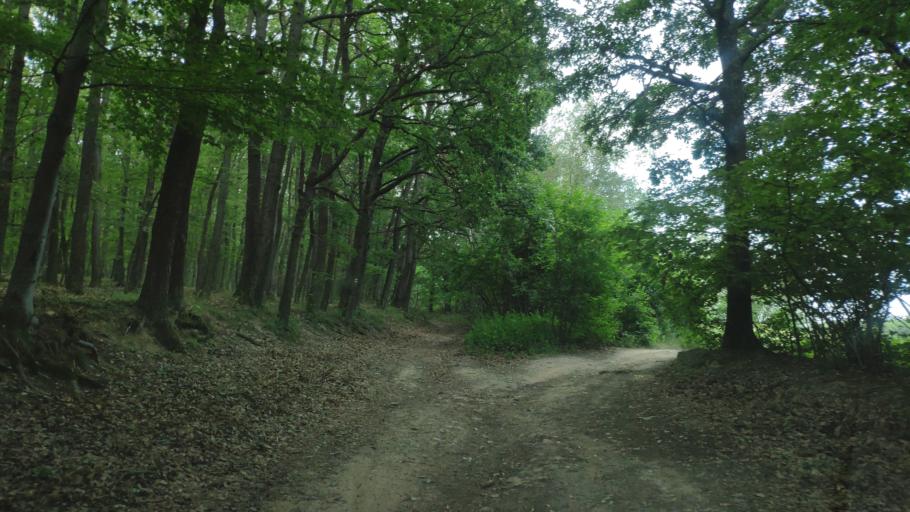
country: SK
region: Kosicky
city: Moldava nad Bodvou
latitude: 48.7172
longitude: 21.0013
